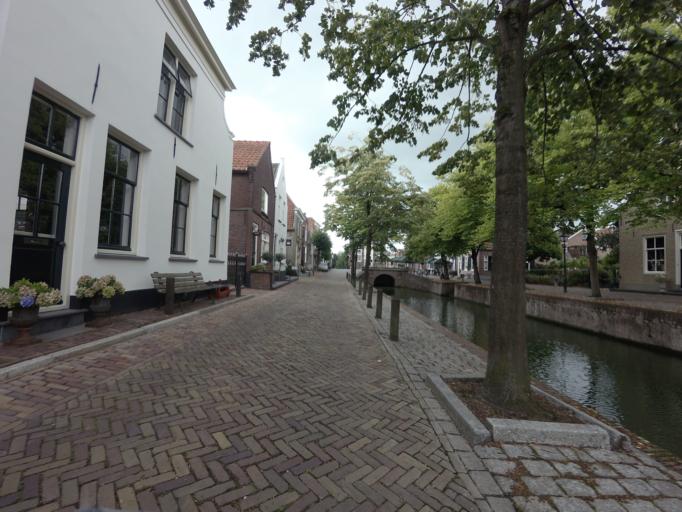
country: NL
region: South Holland
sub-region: Gemeente Schoonhoven
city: Schoonhoven
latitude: 51.9359
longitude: 4.8684
